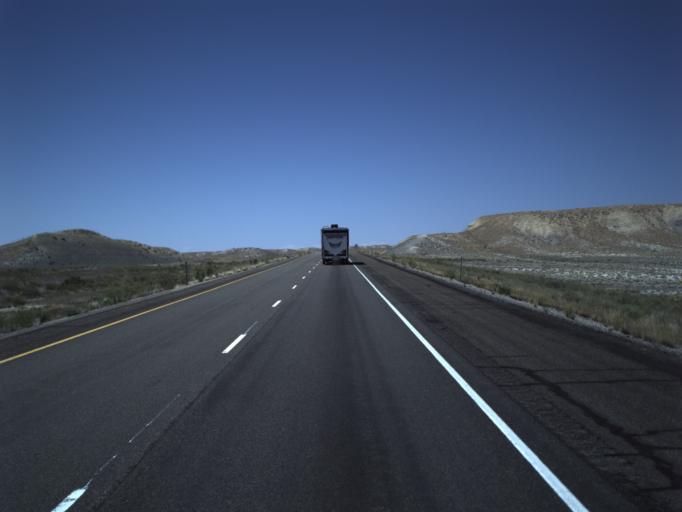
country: US
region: Utah
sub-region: Grand County
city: Moab
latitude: 38.9428
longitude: -109.6263
